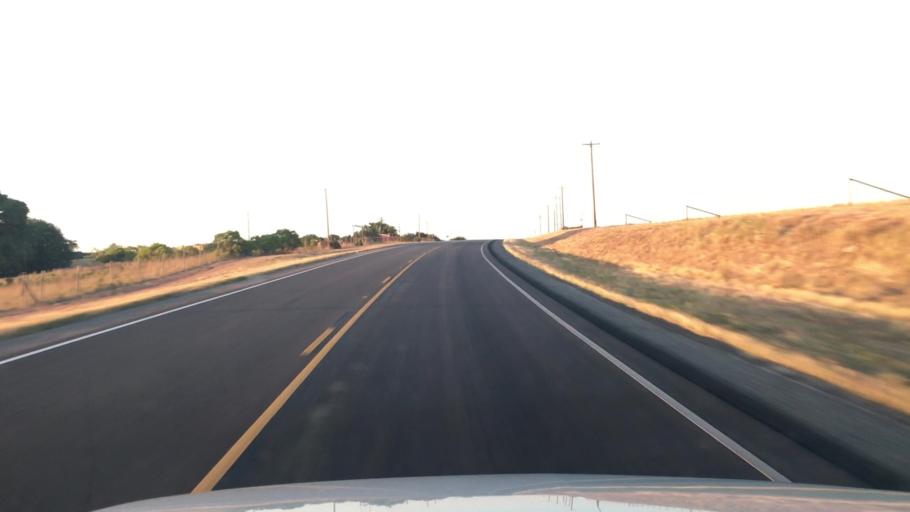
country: US
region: Texas
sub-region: Hamilton County
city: Hico
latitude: 32.0599
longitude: -97.9960
